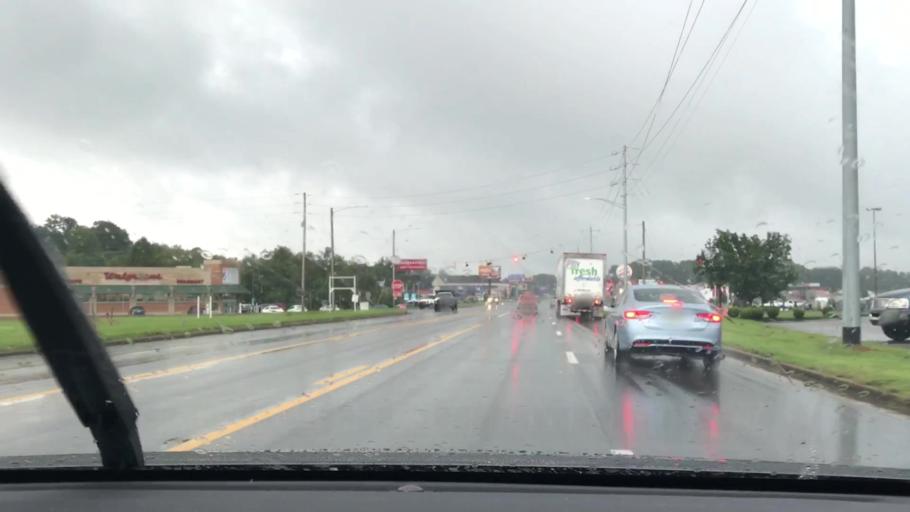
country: US
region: Tennessee
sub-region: Macon County
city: Lafayette
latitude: 36.5230
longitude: -86.0396
